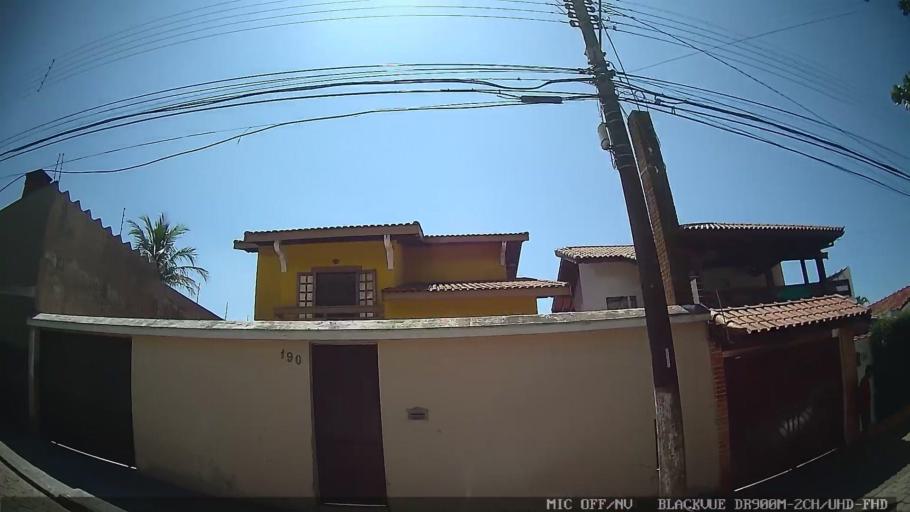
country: BR
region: Sao Paulo
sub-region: Peruibe
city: Peruibe
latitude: -24.3267
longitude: -47.0015
